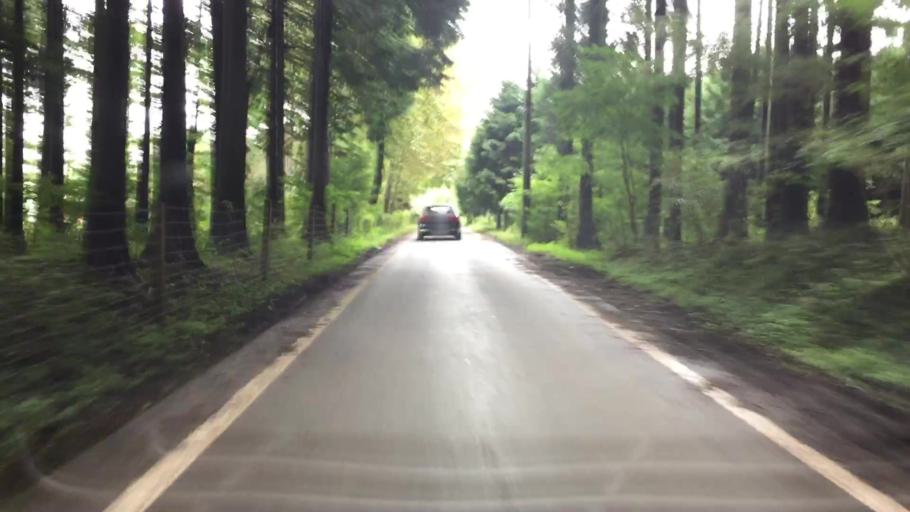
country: JP
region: Yamanashi
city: Fujikawaguchiko
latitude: 35.4001
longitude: 138.5603
